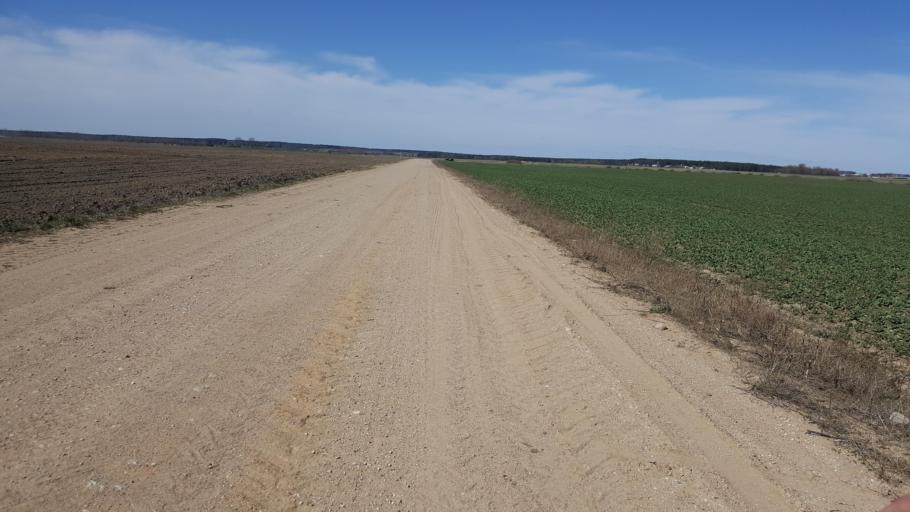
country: BY
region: Brest
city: Zhabinka
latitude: 52.2979
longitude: 23.9109
